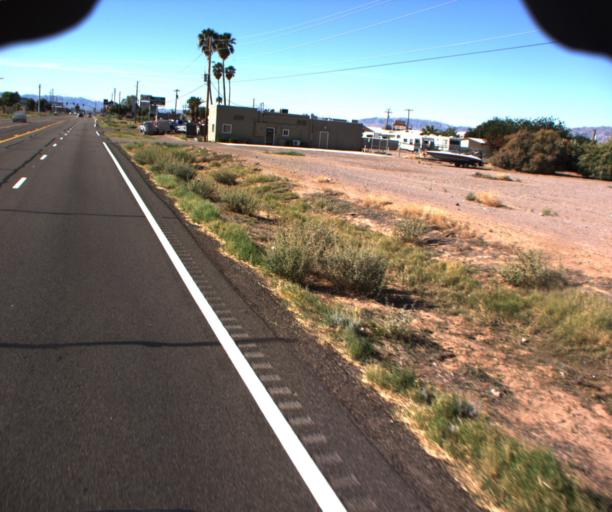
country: US
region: Arizona
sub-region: Mohave County
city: Willow Valley
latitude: 34.9130
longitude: -114.5979
